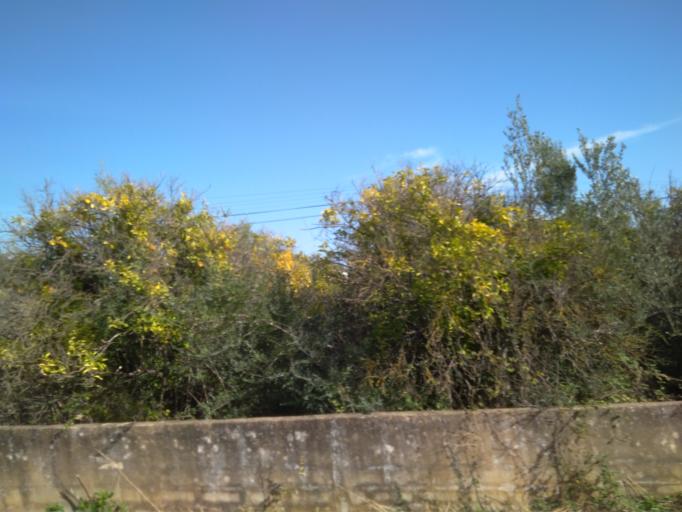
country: PT
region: Faro
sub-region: Faro
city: Santa Barbara de Nexe
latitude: 37.0723
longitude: -7.9592
